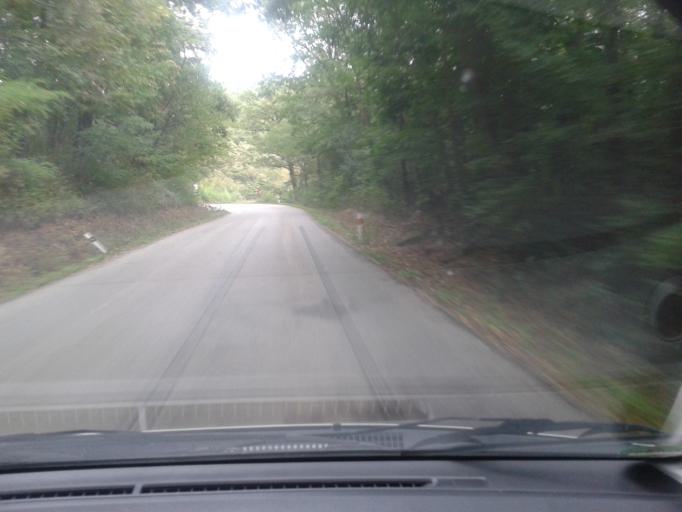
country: SK
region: Nitriansky
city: Zlate Moravce
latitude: 48.4461
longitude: 18.3269
